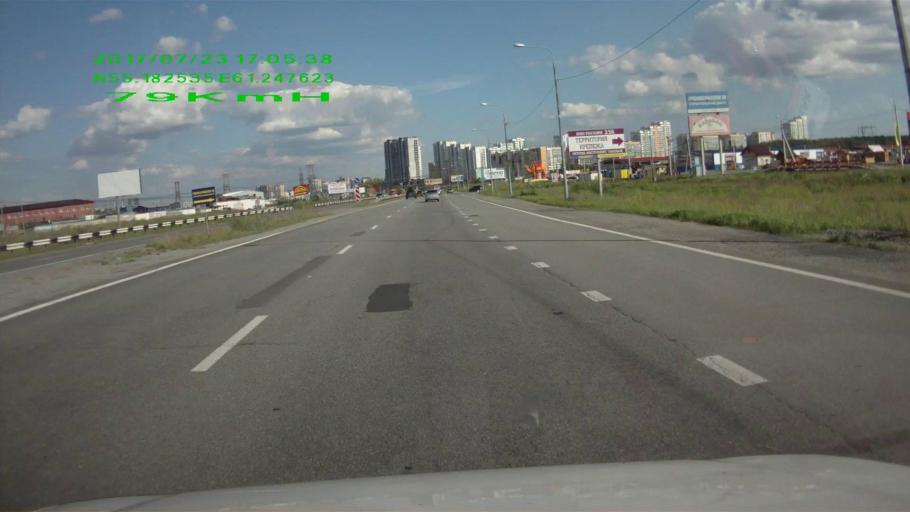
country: RU
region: Chelyabinsk
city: Roshchino
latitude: 55.1819
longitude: 61.2487
